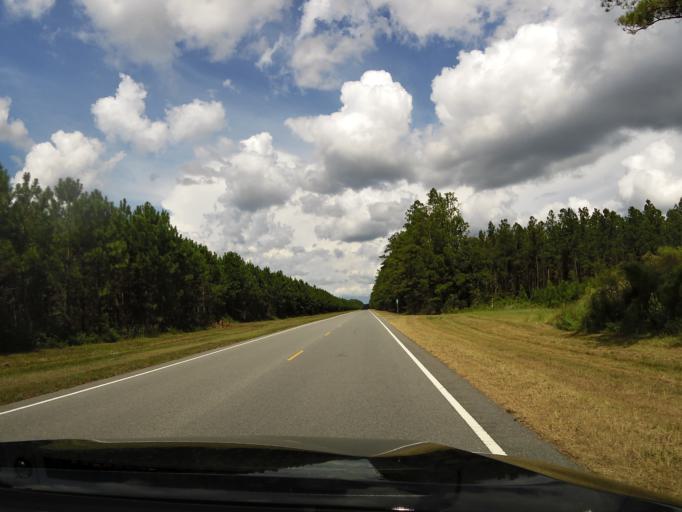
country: US
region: Georgia
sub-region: Charlton County
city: Folkston
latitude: 30.9878
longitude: -82.0258
